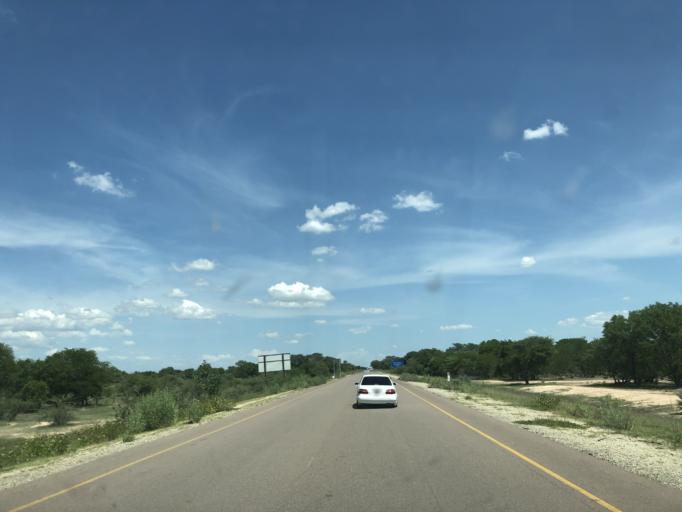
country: AO
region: Cunene
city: Ondjiva
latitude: -16.7943
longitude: 15.4196
